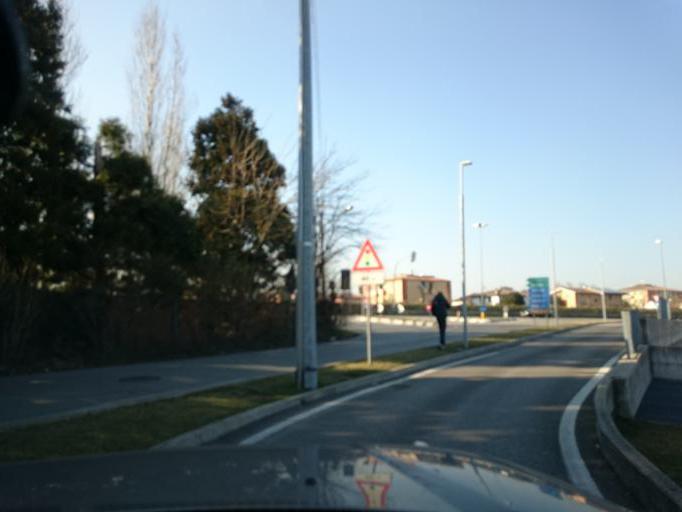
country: IT
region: Veneto
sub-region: Provincia di Padova
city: Mandriola-Sant'Agostino
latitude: 45.3783
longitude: 11.8532
